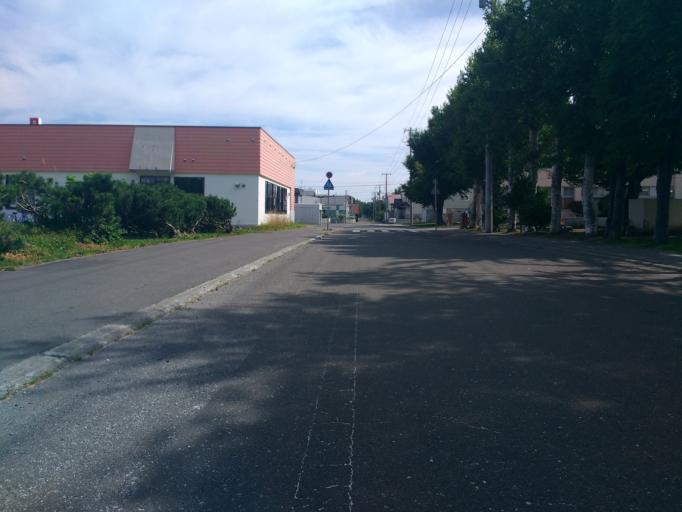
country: JP
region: Hokkaido
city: Ebetsu
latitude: 43.0804
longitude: 141.5004
